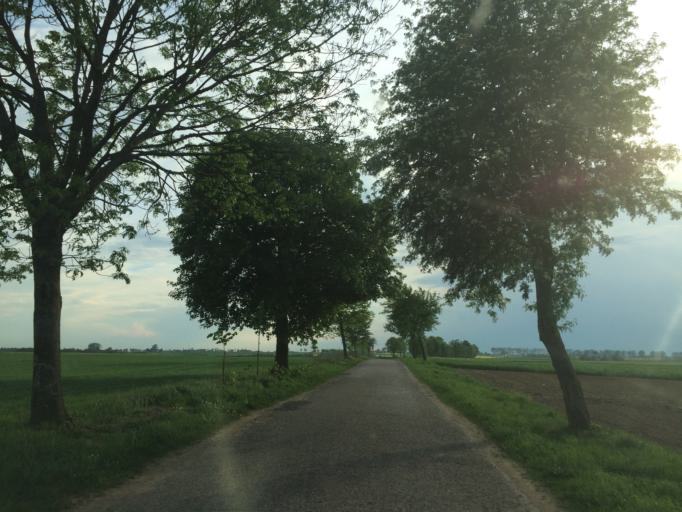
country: PL
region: Kujawsko-Pomorskie
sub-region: Powiat brodnicki
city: Brzozie
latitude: 53.3519
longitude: 19.5953
